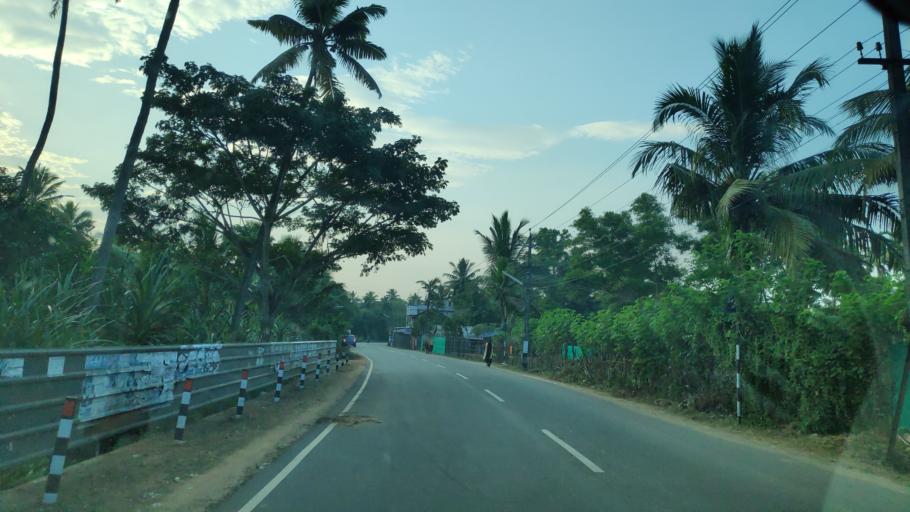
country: IN
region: Kerala
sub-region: Alappuzha
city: Shertallai
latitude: 9.6759
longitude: 76.3826
